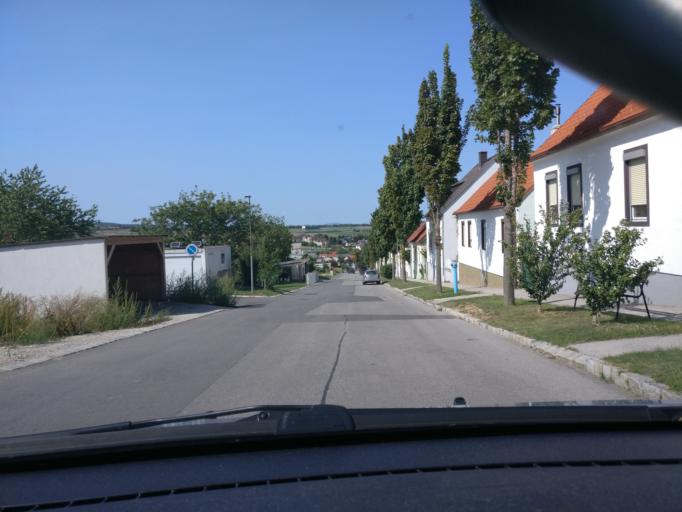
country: AT
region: Burgenland
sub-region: Politischer Bezirk Mattersburg
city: Mattersburg
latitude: 47.7291
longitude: 16.3939
